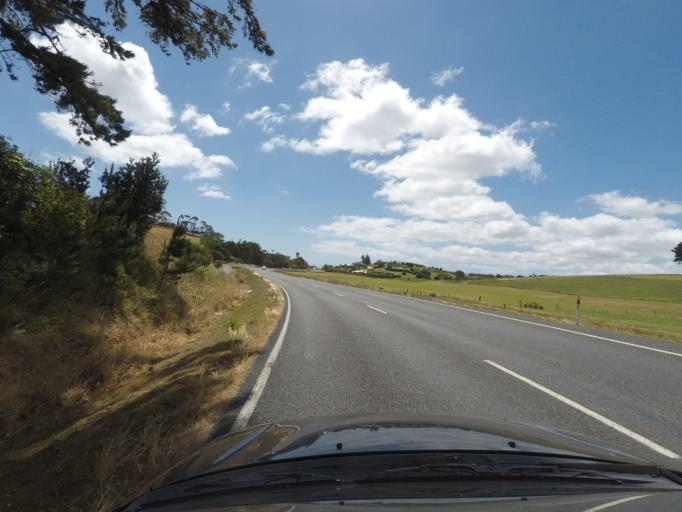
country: NZ
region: Northland
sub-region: Whangarei
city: Ruakaka
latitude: -35.9938
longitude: 174.4636
